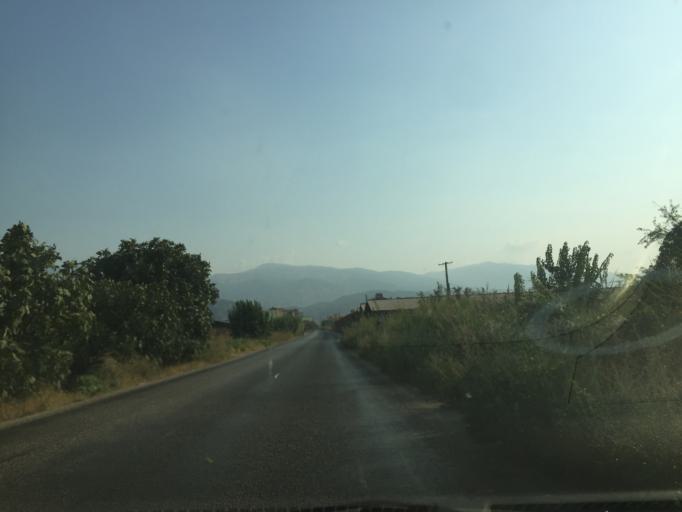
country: TR
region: Manisa
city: Salihli
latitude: 38.5004
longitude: 28.1847
